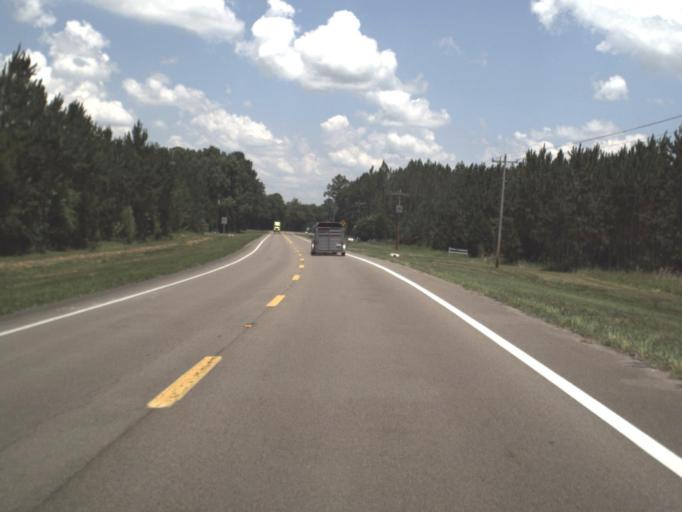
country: US
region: Florida
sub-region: Union County
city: Lake Butler
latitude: 29.9130
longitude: -82.4240
